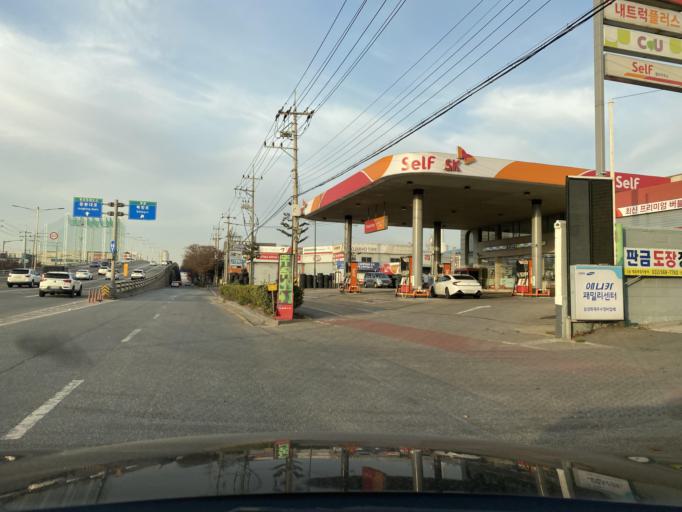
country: KR
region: Incheon
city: Incheon
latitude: 37.5041
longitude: 126.6486
